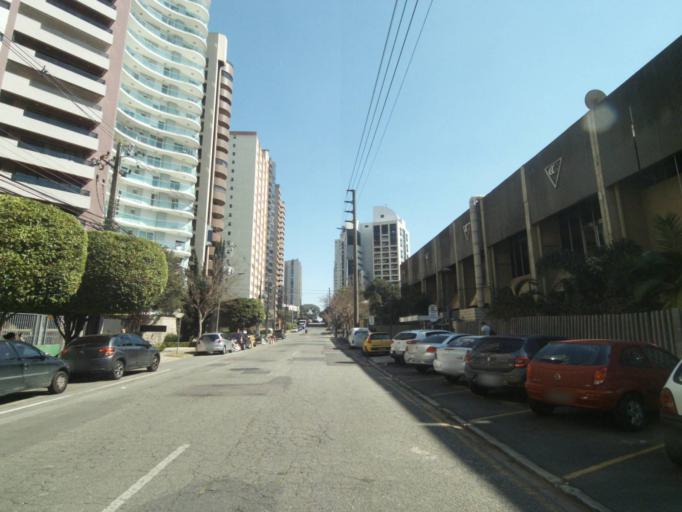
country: BR
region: Parana
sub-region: Curitiba
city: Curitiba
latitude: -25.4519
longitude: -49.2858
